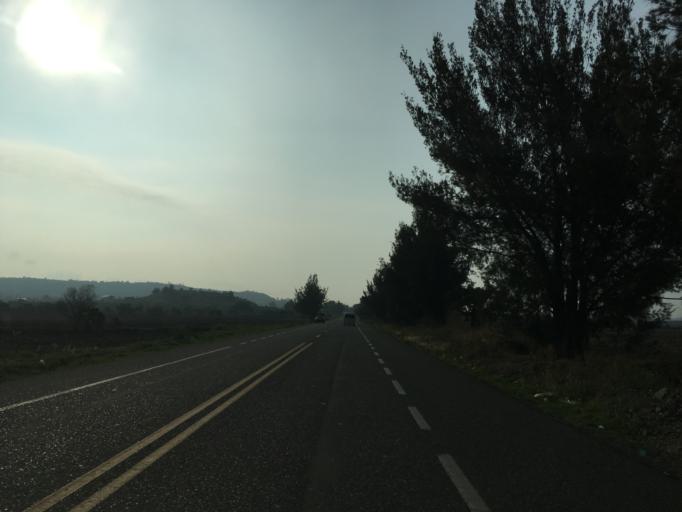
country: MX
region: Oaxaca
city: San Andres Sinaxtla
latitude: 17.4670
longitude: -97.2671
